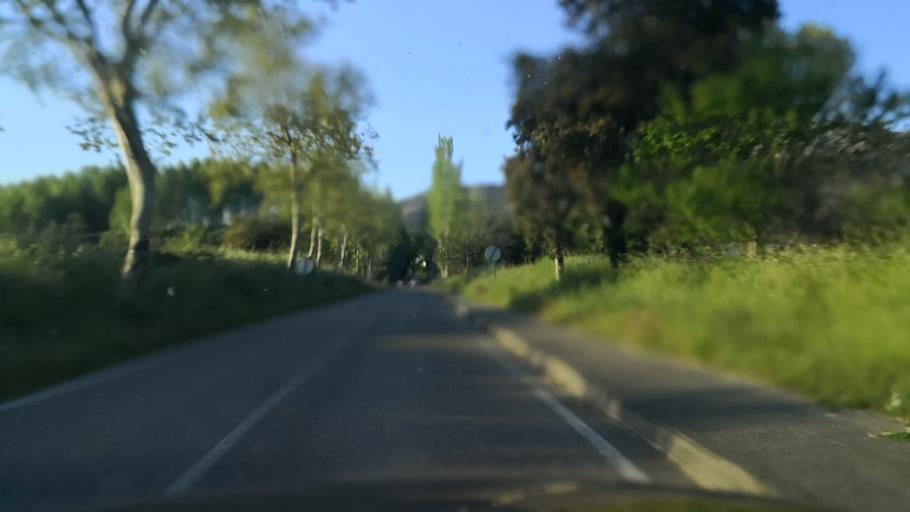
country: PT
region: Portalegre
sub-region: Marvao
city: Marvao
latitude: 39.3785
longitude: -7.3883
